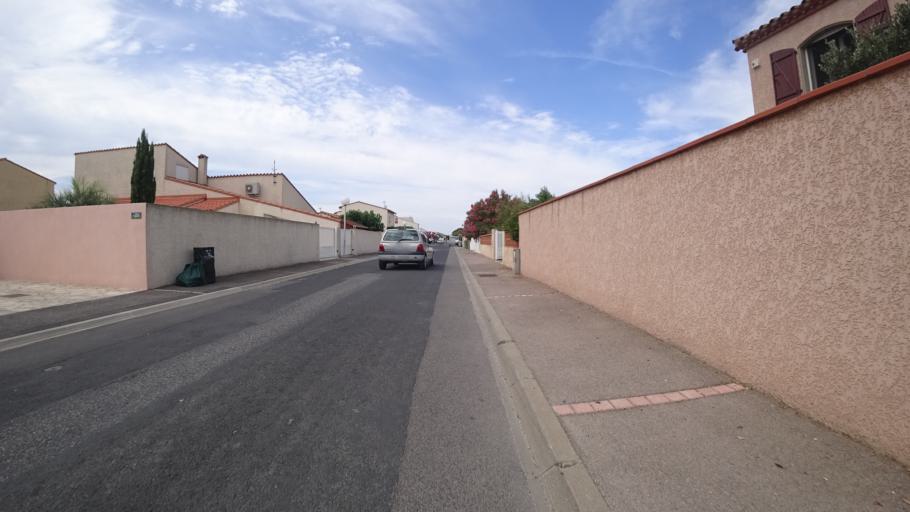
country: FR
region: Languedoc-Roussillon
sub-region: Departement des Pyrenees-Orientales
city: Le Barcares
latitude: 42.7944
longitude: 3.0317
